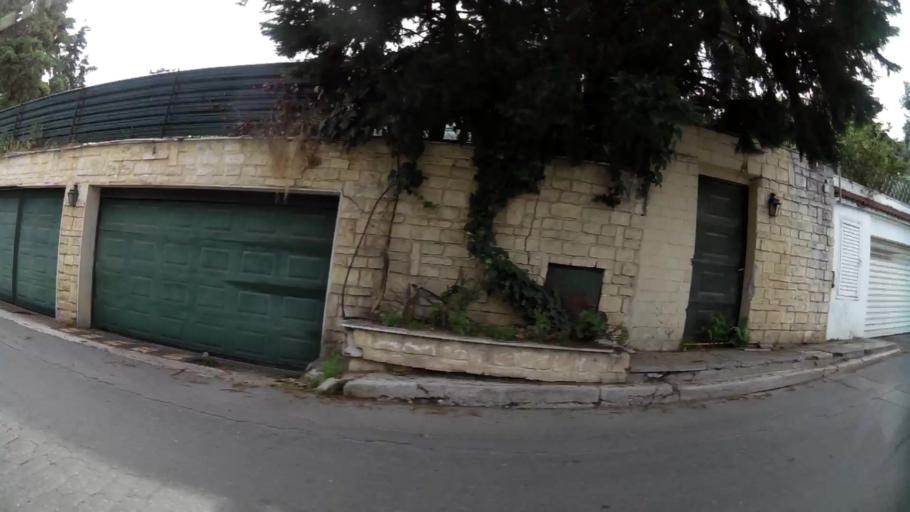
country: GR
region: Central Macedonia
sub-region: Nomos Thessalonikis
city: Panorama
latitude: 40.5840
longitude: 23.0206
